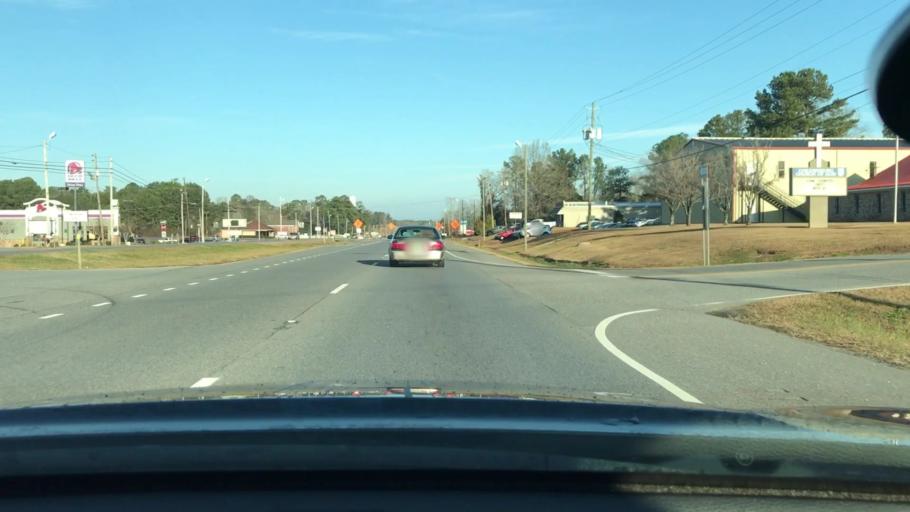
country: US
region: Alabama
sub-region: Talladega County
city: Childersburg
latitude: 33.2673
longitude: -86.3525
